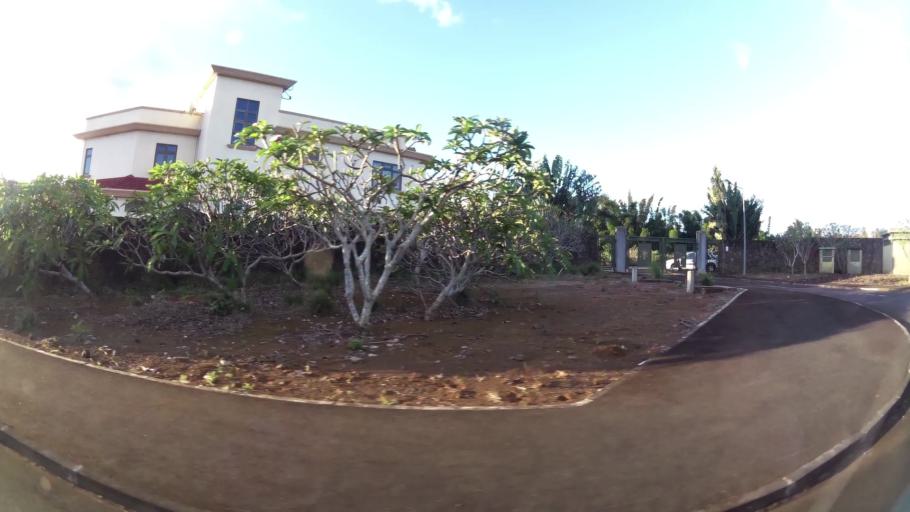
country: MU
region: Plaines Wilhems
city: Ebene
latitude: -20.2379
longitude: 57.4835
